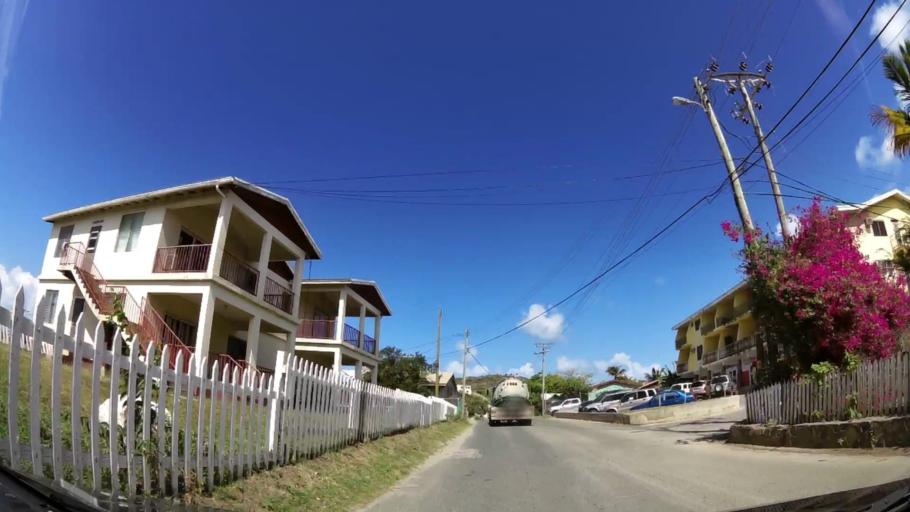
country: VG
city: Tortola
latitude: 18.4525
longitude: -64.4305
